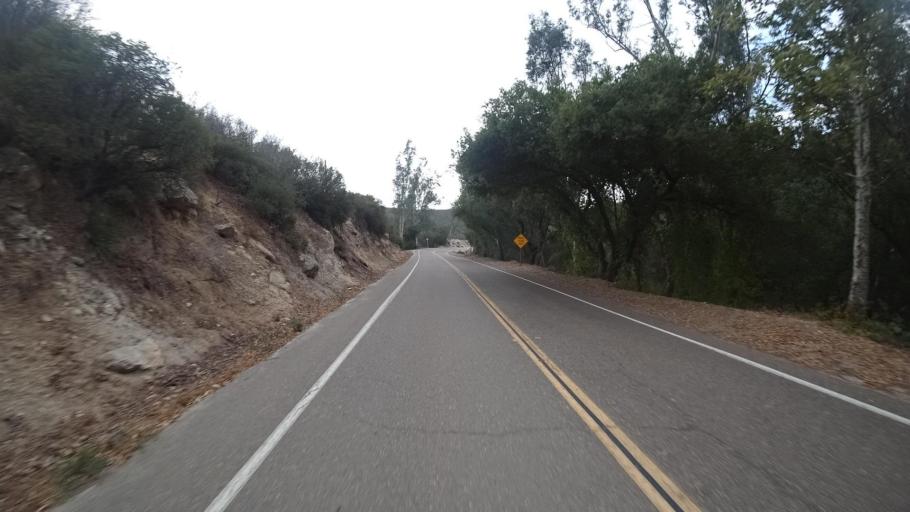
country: US
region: California
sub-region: San Diego County
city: Eucalyptus Hills
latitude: 32.9616
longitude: -116.9113
